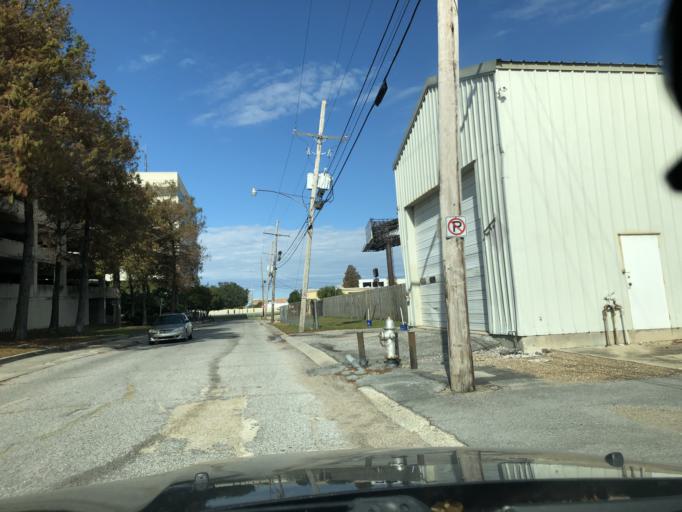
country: US
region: Louisiana
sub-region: Jefferson Parish
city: Metairie
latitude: 29.9961
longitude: -90.1625
